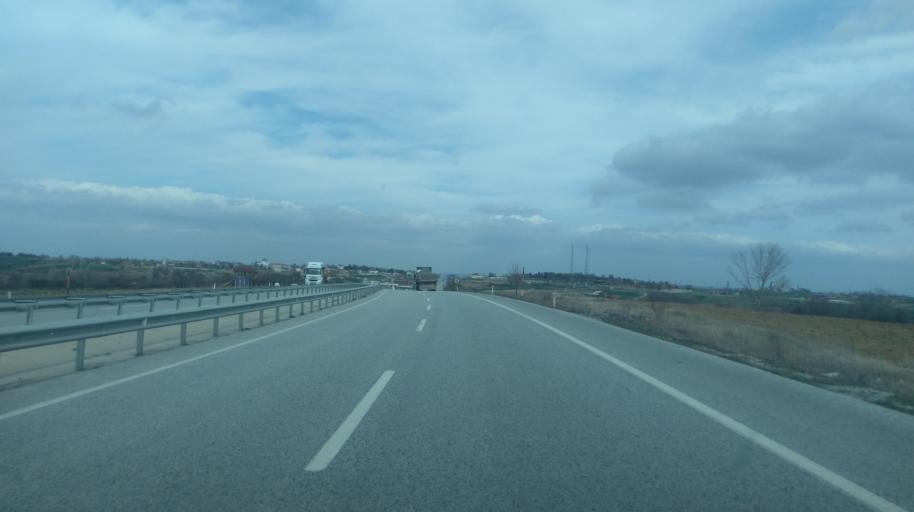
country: TR
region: Edirne
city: Kircasalih
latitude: 41.3820
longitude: 26.7903
